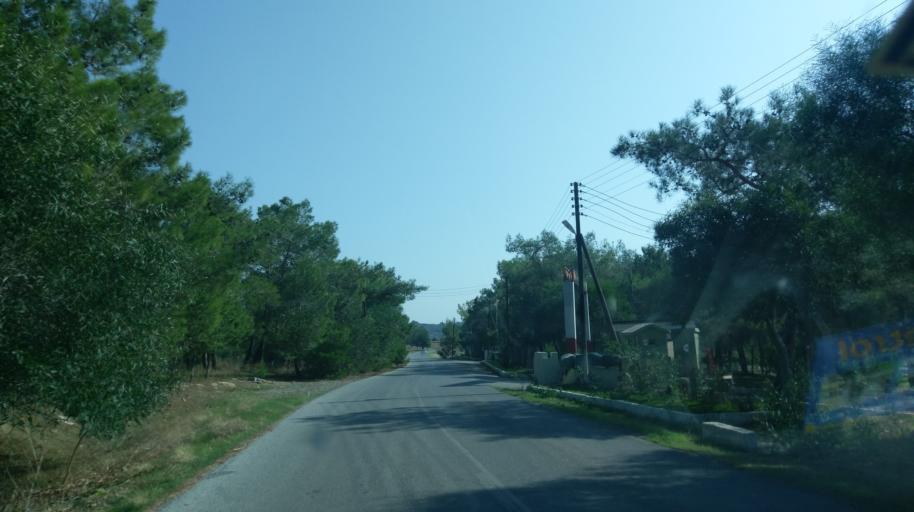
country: CY
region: Keryneia
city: Lapithos
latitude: 35.3266
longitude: 33.0439
